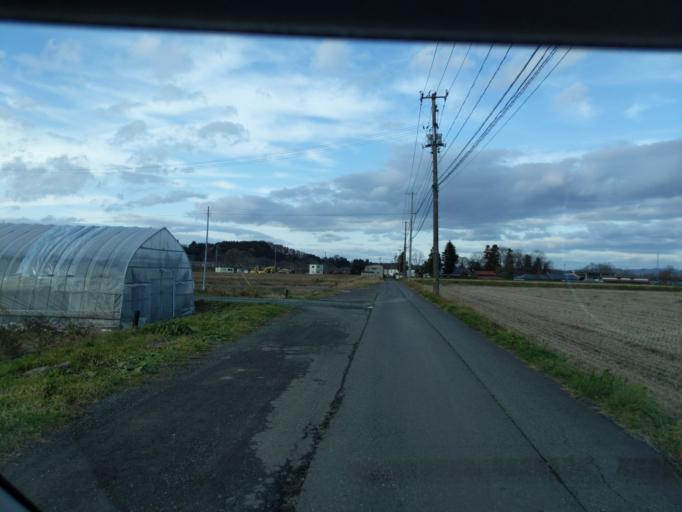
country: JP
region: Iwate
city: Mizusawa
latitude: 39.1602
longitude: 141.0892
